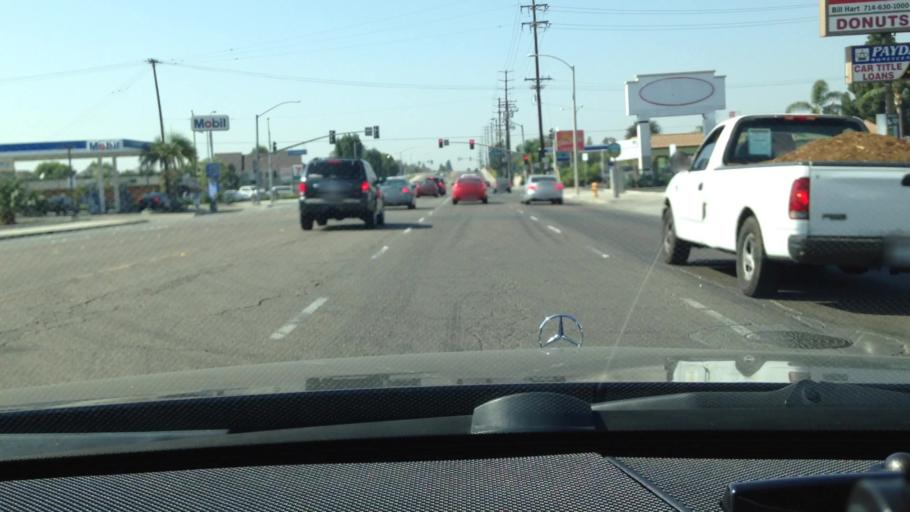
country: US
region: California
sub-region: Orange County
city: Placentia
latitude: 33.8370
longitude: -117.8704
